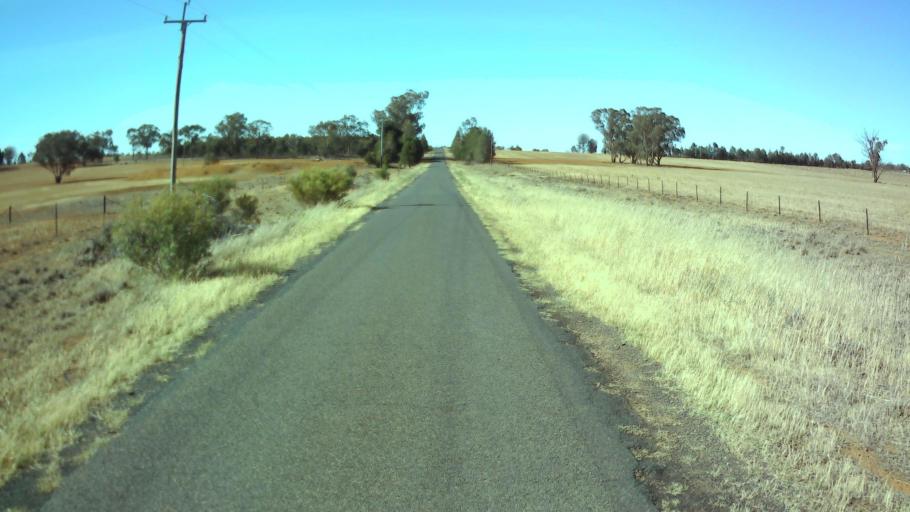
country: AU
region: New South Wales
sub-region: Weddin
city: Grenfell
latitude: -33.7599
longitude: 147.8297
